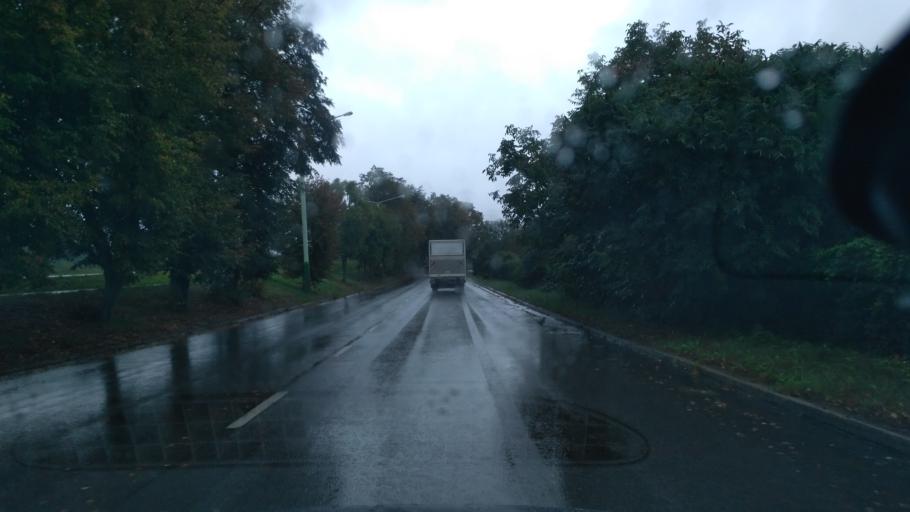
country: PL
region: Subcarpathian Voivodeship
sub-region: Powiat debicki
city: Debica
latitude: 50.0597
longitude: 21.3917
